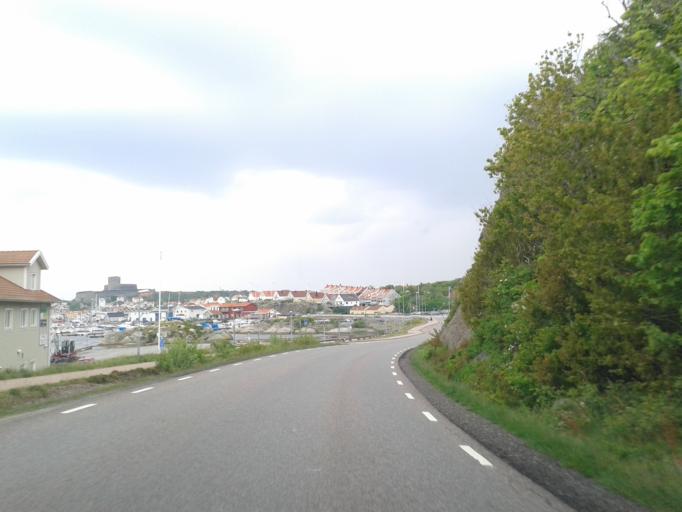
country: SE
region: Vaestra Goetaland
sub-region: Kungalvs Kommun
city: Marstrand
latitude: 57.8879
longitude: 11.6023
